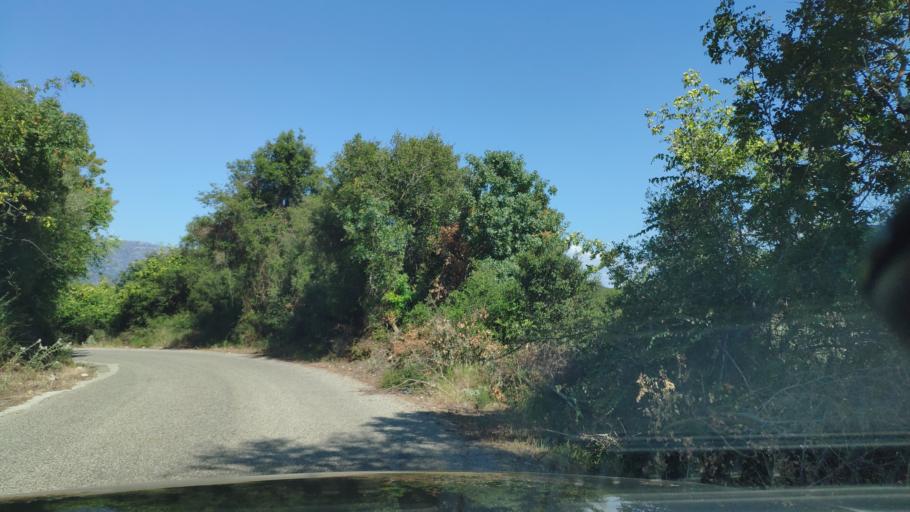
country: GR
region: West Greece
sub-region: Nomos Aitolias kai Akarnanias
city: Katouna
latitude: 38.7503
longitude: 21.1471
